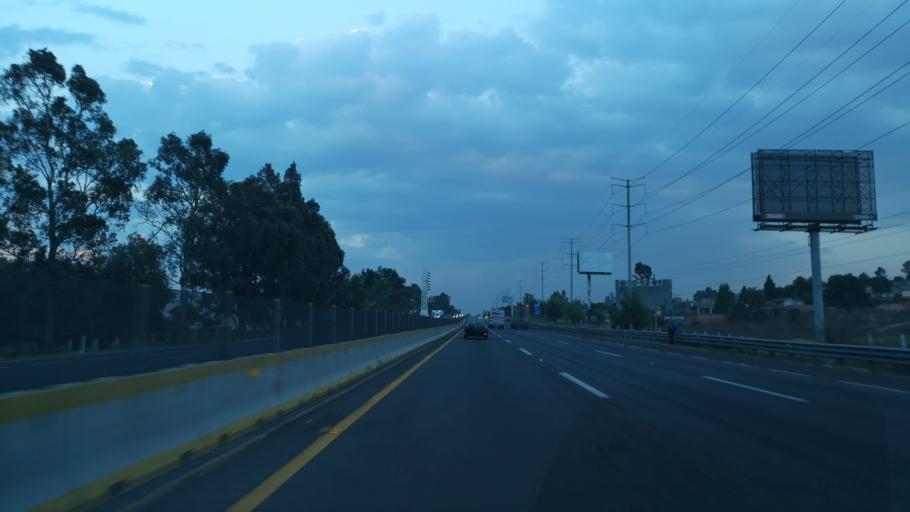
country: MX
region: Puebla
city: Ocotlan
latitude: 19.1511
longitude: -98.2876
